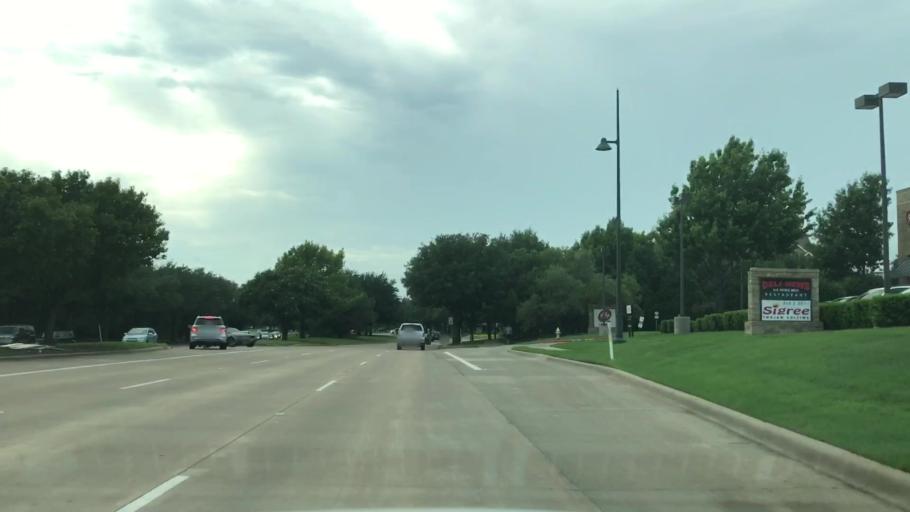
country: US
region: Texas
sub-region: Collin County
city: Frisco
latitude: 33.1092
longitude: -96.8071
